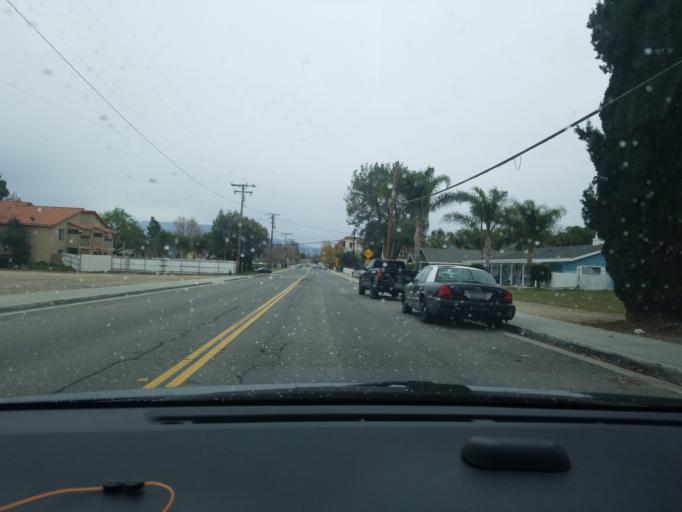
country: US
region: California
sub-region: Riverside County
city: Temecula
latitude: 33.4922
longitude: -117.1517
